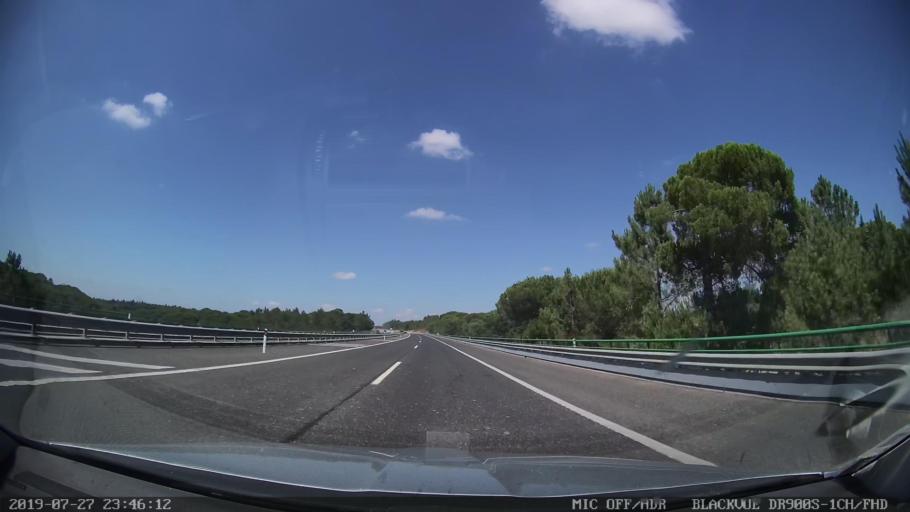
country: PT
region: Evora
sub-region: Vendas Novas
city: Vendas Novas
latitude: 38.6356
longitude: -8.4990
